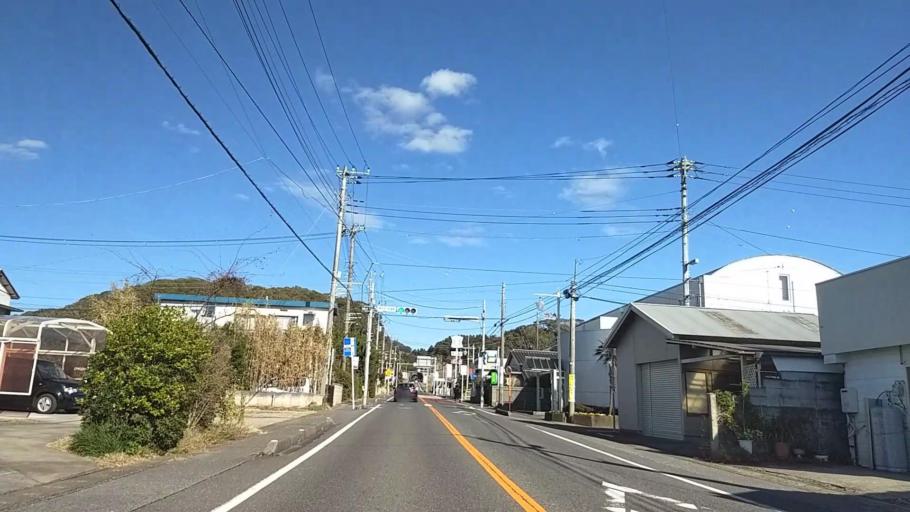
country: JP
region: Chiba
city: Ohara
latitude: 35.1915
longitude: 140.3606
